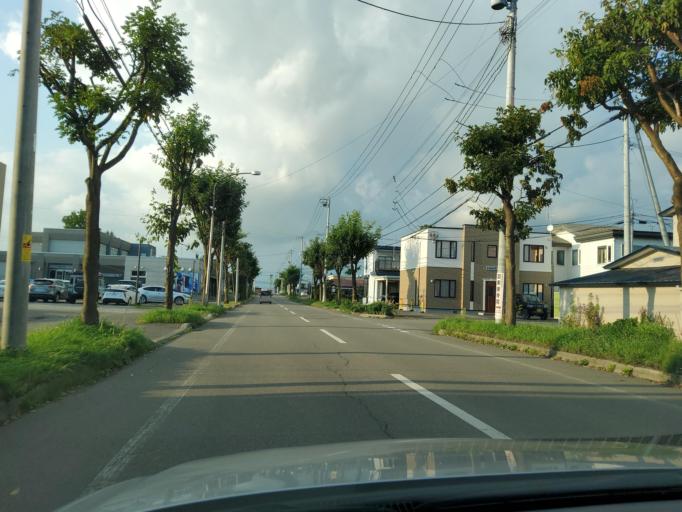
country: JP
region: Hokkaido
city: Obihiro
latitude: 42.9181
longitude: 143.1849
